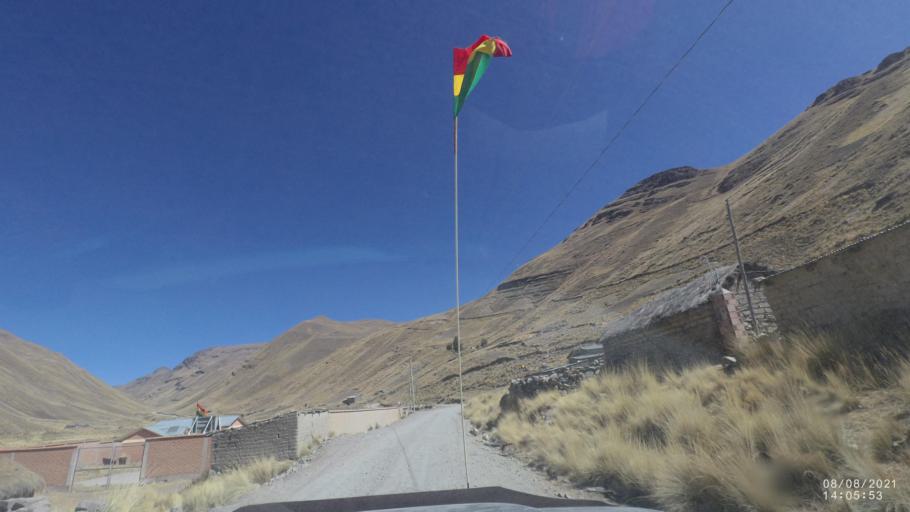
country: BO
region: Cochabamba
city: Sipe Sipe
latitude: -17.1205
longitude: -66.4405
